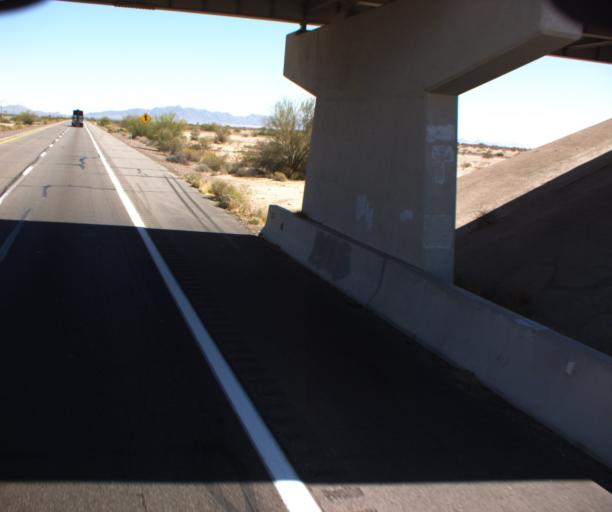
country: US
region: Arizona
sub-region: Yuma County
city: Wellton
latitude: 32.6934
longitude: -113.9533
